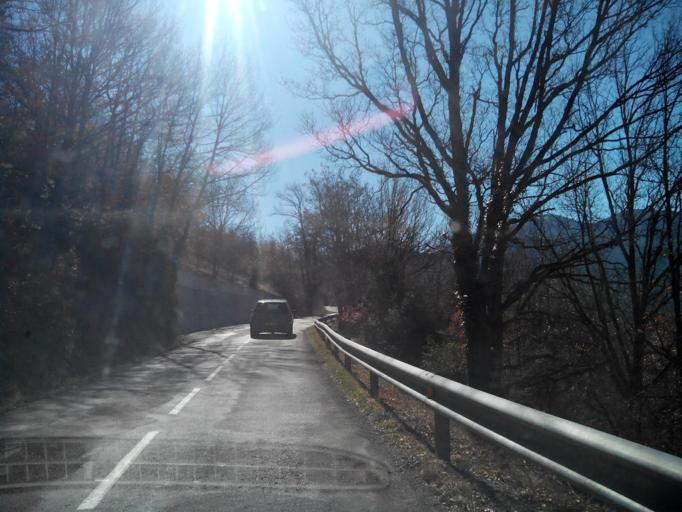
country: ES
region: Catalonia
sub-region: Provincia de Lleida
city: Lles de Cerdanya
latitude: 42.3676
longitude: 1.6850
